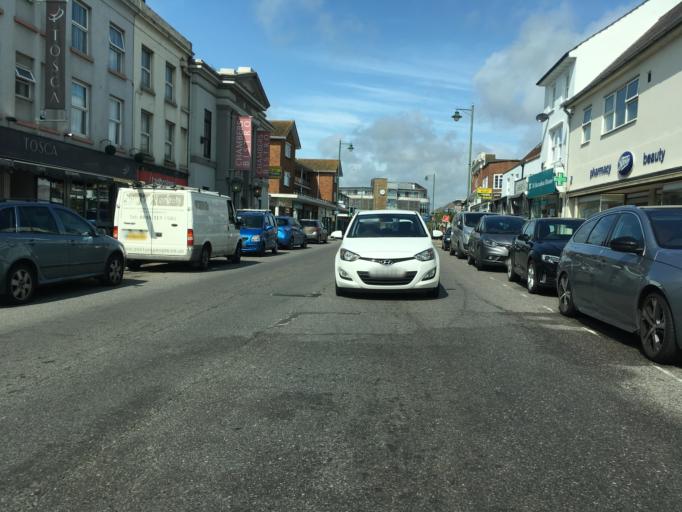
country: GB
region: England
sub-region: West Sussex
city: Shoreham-by-Sea
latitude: 50.8319
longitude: -0.2762
